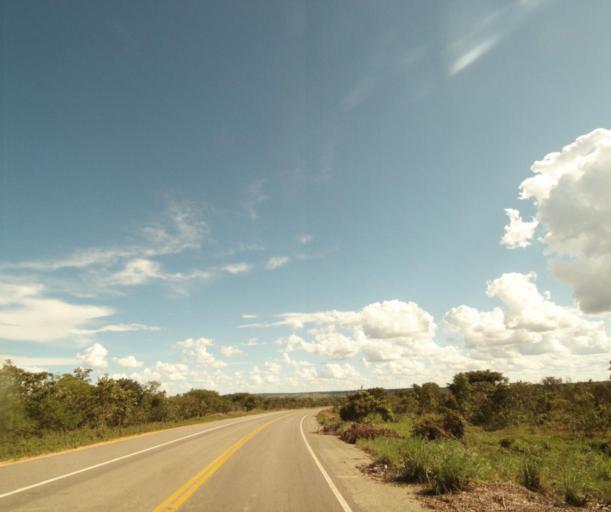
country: BR
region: Bahia
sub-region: Correntina
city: Correntina
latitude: -13.3105
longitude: -44.6416
